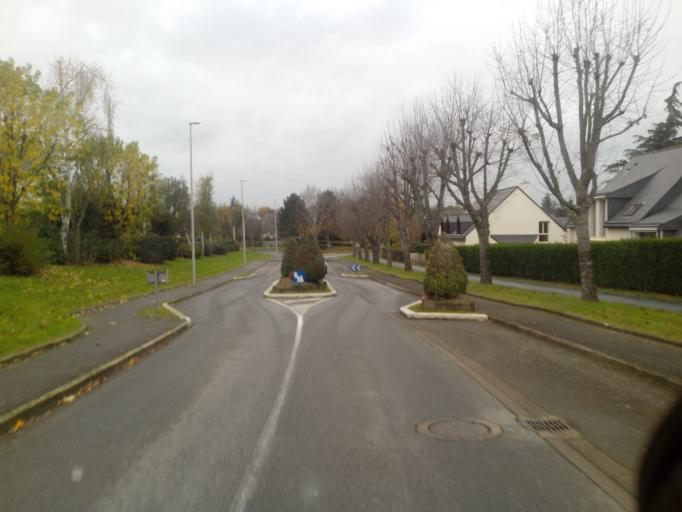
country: FR
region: Brittany
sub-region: Departement d'Ille-et-Vilaine
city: Cesson-Sevigne
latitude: 48.1239
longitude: -1.6116
